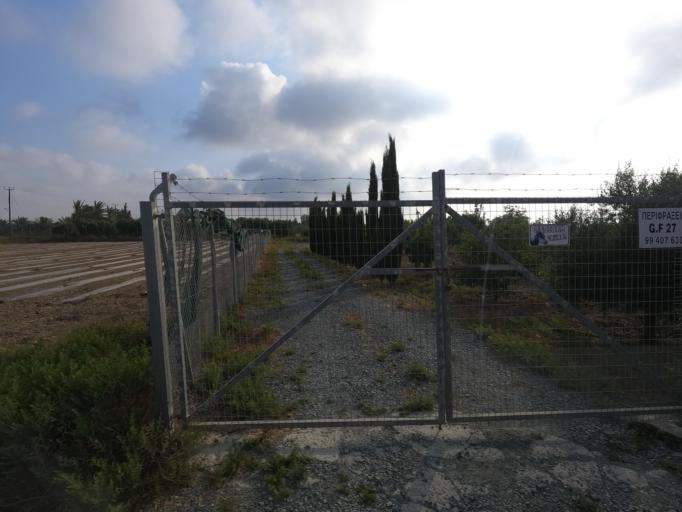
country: CY
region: Larnaka
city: Tersefanou
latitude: 34.8274
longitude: 33.5537
